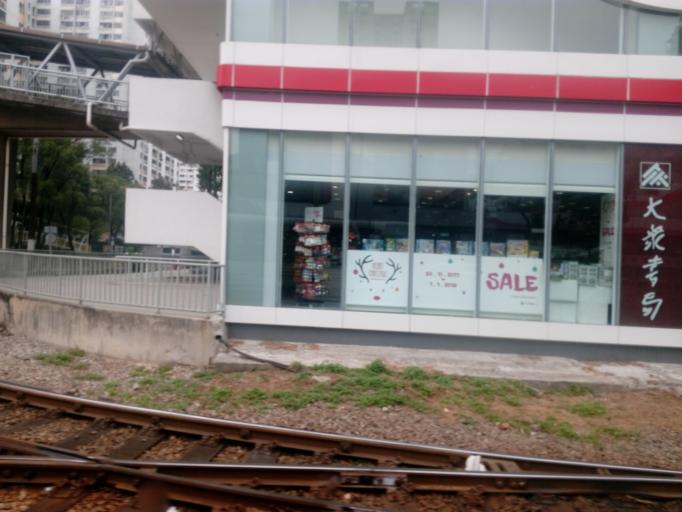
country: HK
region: Tuen Mun
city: Tuen Mun
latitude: 22.3870
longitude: 113.9750
